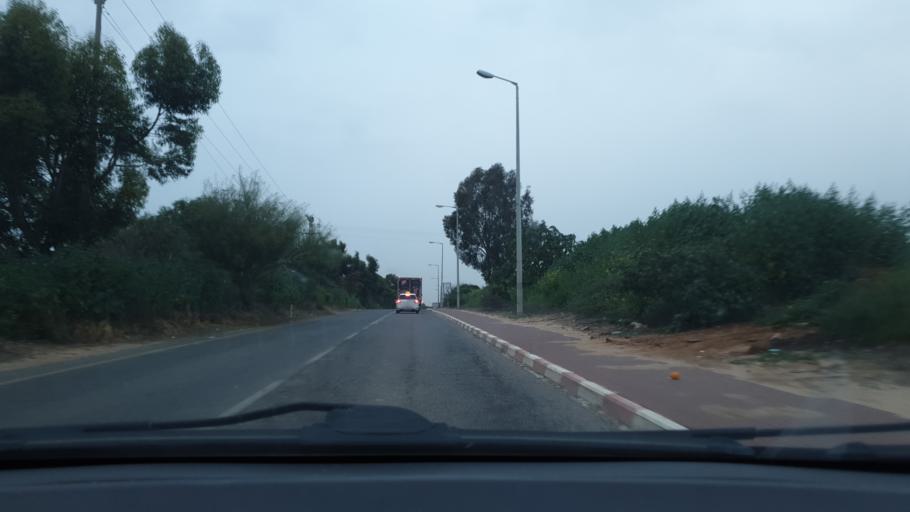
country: IL
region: Central District
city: Kefar Habad
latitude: 31.9815
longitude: 34.8394
